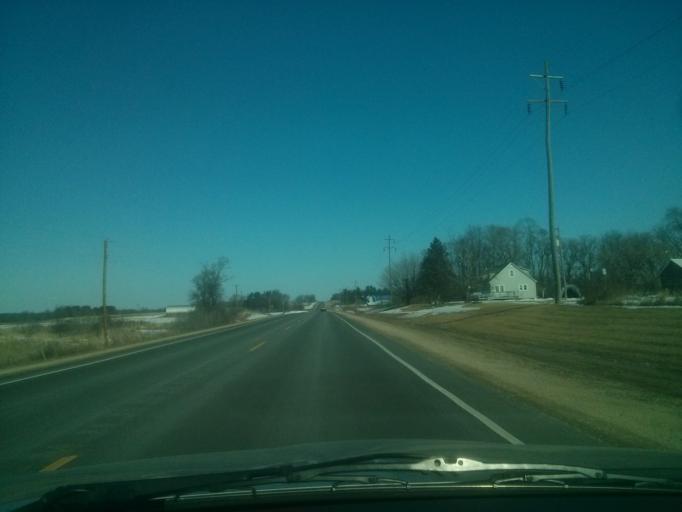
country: US
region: Wisconsin
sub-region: Polk County
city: Clear Lake
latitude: 45.1461
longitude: -92.2819
